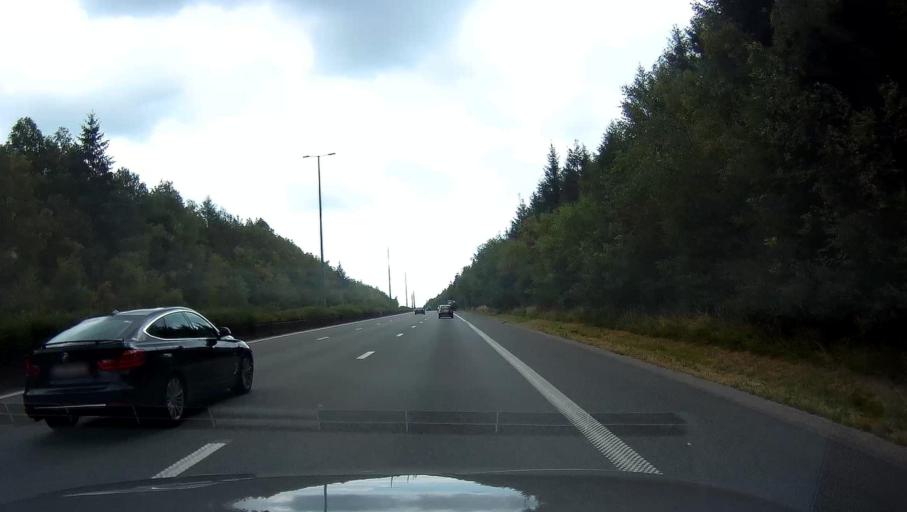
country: BE
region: Wallonia
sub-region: Province du Luxembourg
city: Tellin
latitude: 50.0687
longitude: 5.1866
